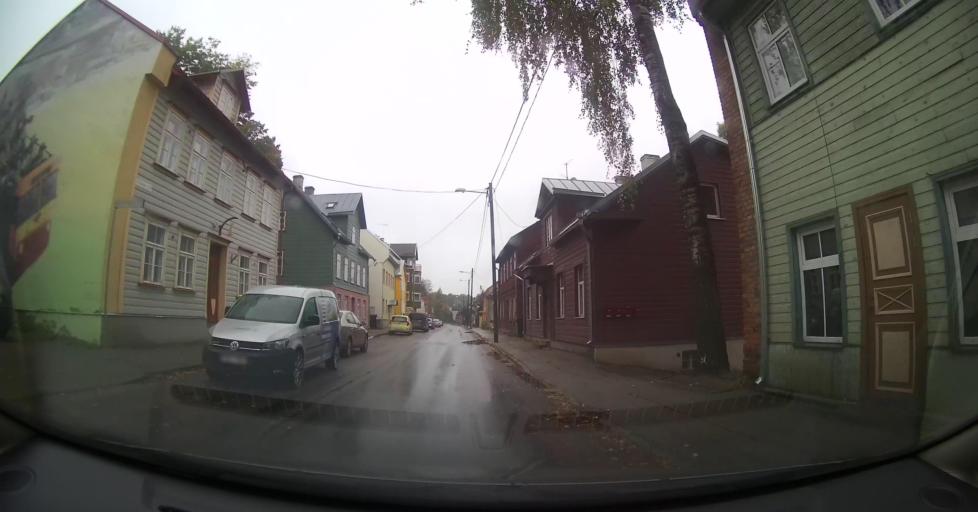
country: EE
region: Tartu
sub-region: Tartu linn
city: Tartu
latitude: 58.3850
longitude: 26.7105
